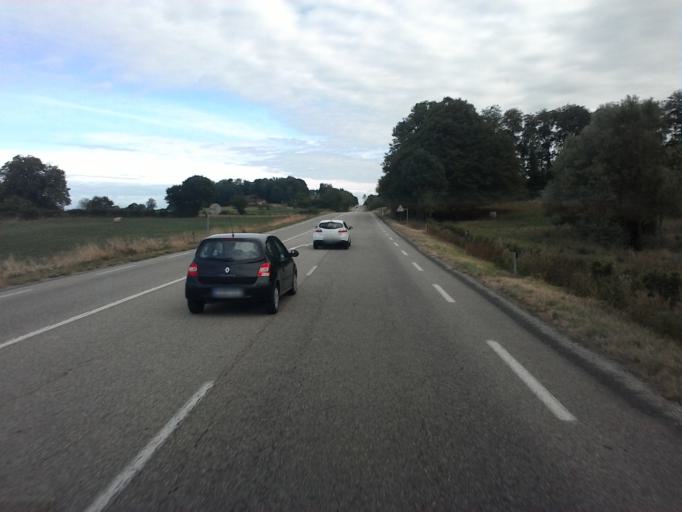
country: FR
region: Rhone-Alpes
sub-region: Departement de l'Ain
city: Saint-Martin-du-Mont
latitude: 46.0761
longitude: 5.3223
